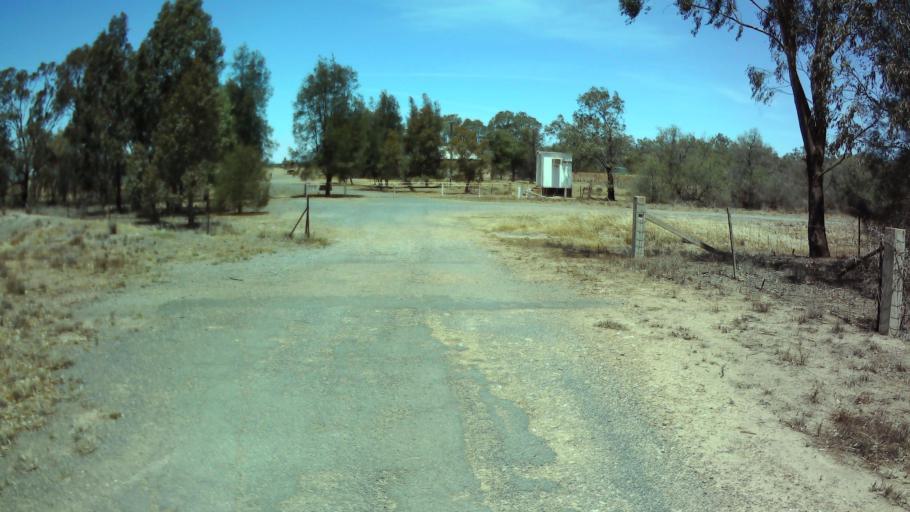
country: AU
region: New South Wales
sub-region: Bland
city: West Wyalong
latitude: -33.7593
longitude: 147.5253
